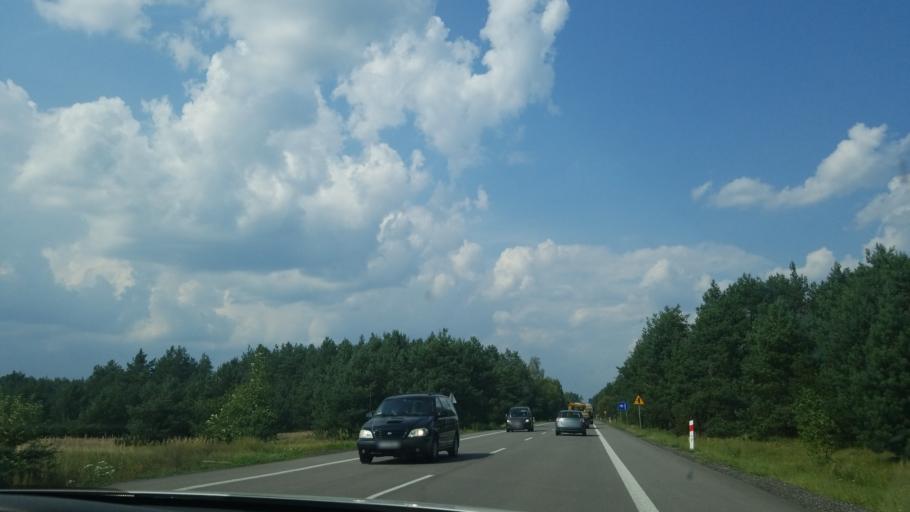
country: PL
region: Subcarpathian Voivodeship
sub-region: Powiat nizanski
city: Jarocin
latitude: 50.6263
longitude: 22.2866
